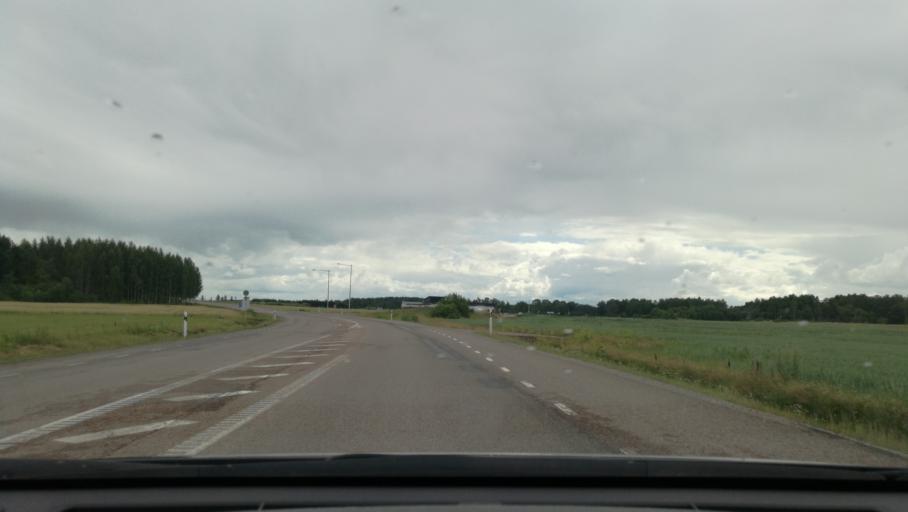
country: SE
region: Vaestmanland
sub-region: Kopings Kommun
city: Koping
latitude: 59.4855
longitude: 15.9849
